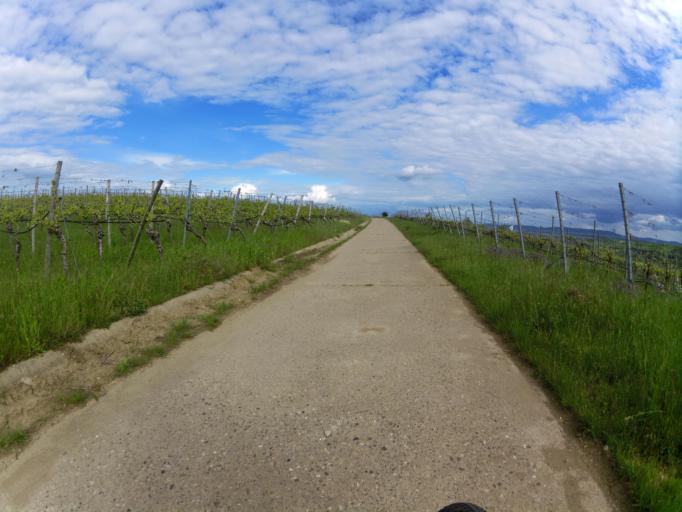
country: DE
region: Bavaria
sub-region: Regierungsbezirk Unterfranken
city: Sommerach
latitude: 49.8380
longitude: 10.1932
